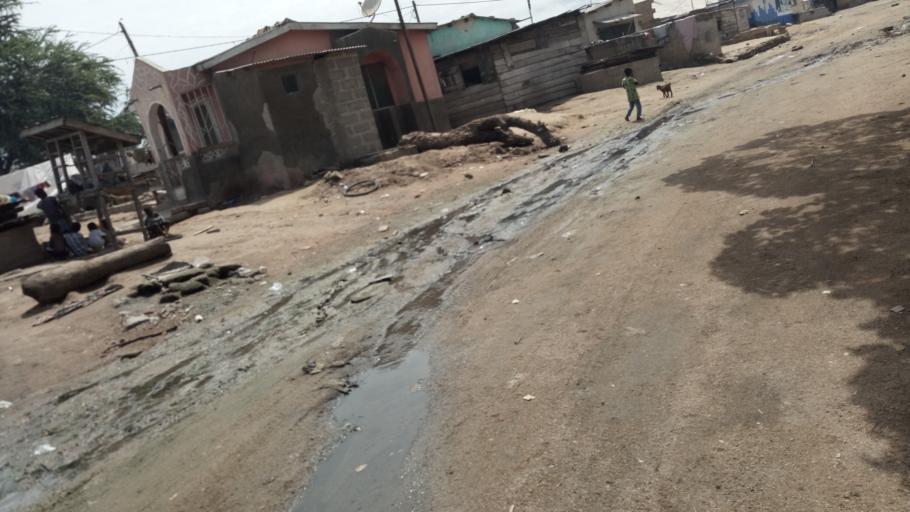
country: GH
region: Central
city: Winneba
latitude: 5.3487
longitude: -0.6179
